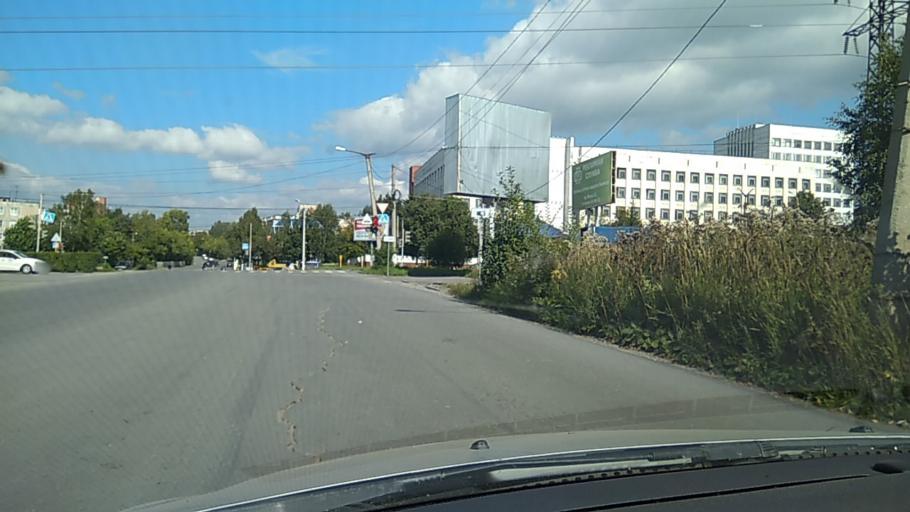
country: RU
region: Chelyabinsk
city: Zlatoust
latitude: 55.1129
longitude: 59.7061
